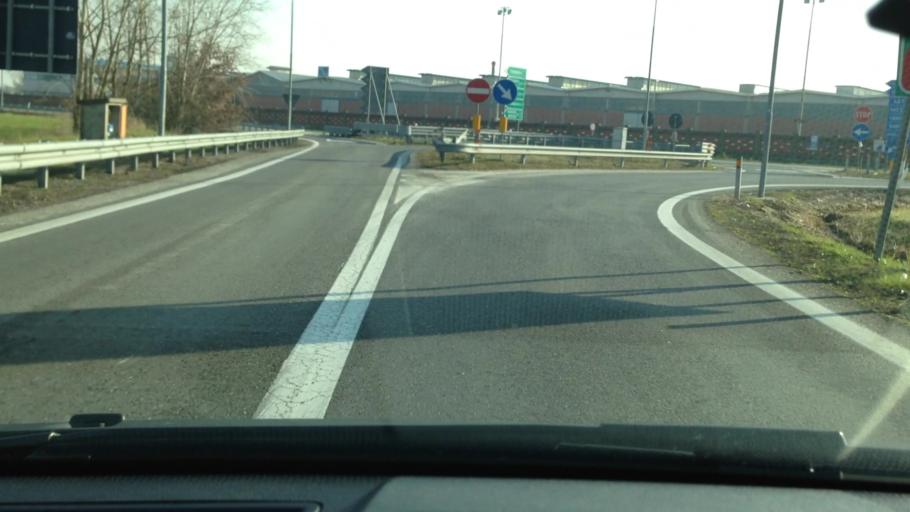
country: IT
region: Piedmont
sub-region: Provincia di Alessandria
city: Quattordio
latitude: 44.9002
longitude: 8.4204
